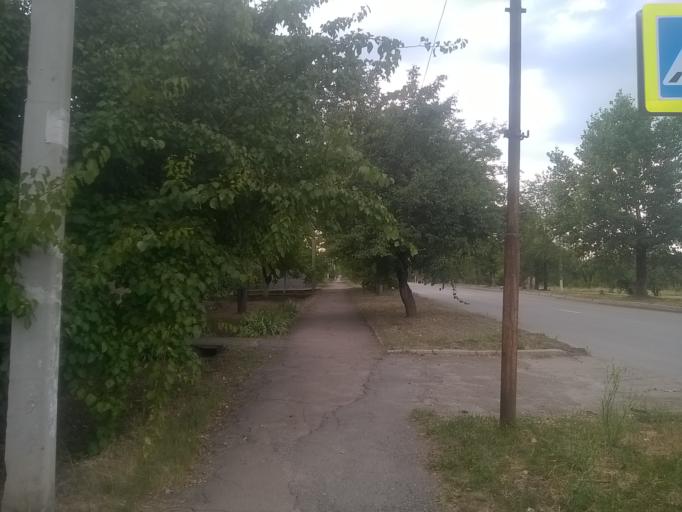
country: RU
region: Rostov
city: Donetsk
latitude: 48.3313
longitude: 39.9628
